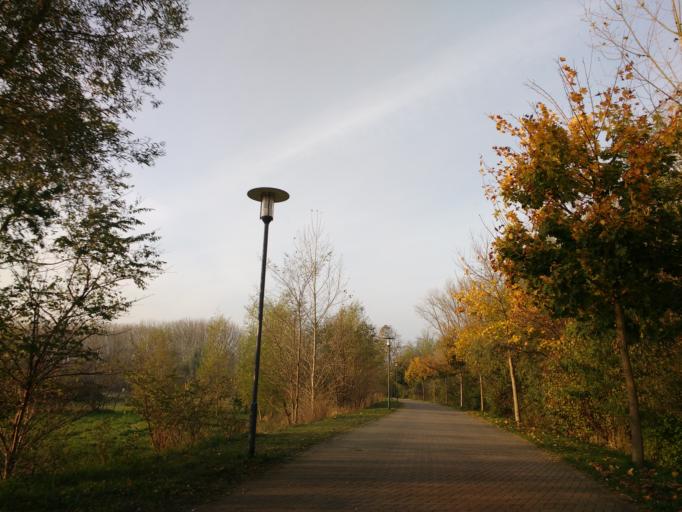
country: DE
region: Mecklenburg-Vorpommern
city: Ostseebad Boltenhagen
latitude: 53.9757
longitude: 11.2473
